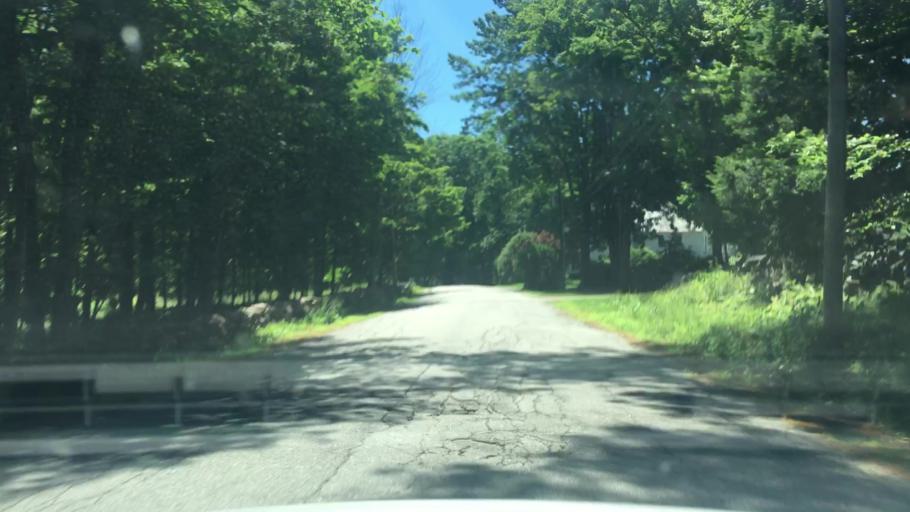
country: US
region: New Hampshire
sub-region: Merrimack County
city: Hopkinton
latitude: 43.2121
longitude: -71.6712
